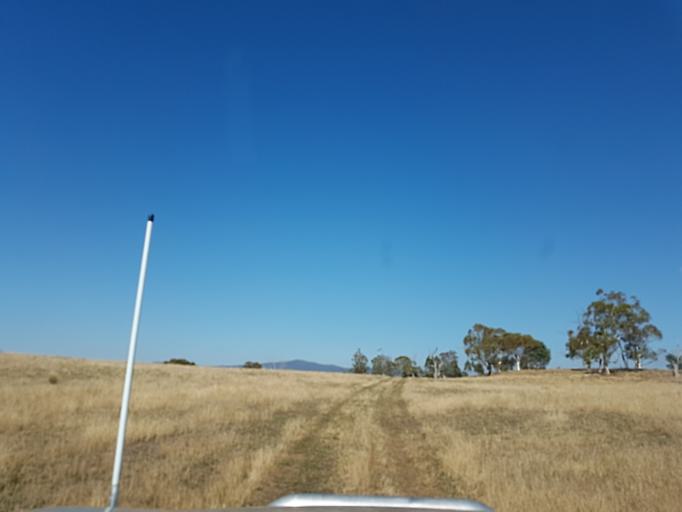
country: AU
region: New South Wales
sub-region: Snowy River
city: Jindabyne
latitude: -37.0481
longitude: 148.2932
